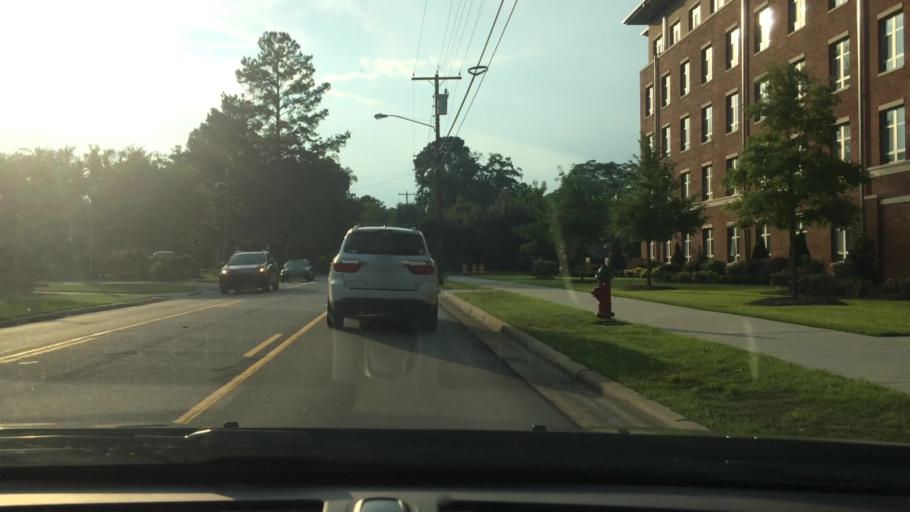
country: US
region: North Carolina
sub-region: Pitt County
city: Greenville
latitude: 35.5994
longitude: -77.3648
